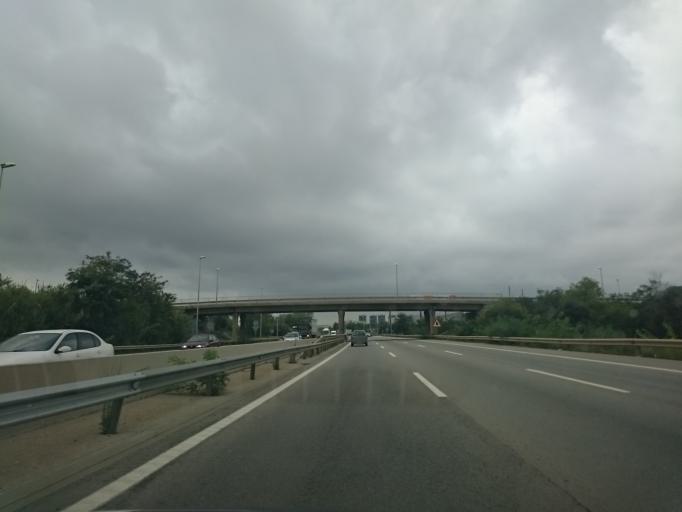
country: ES
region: Catalonia
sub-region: Provincia de Barcelona
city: Sant Boi de Llobregat
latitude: 41.3204
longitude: 2.0396
